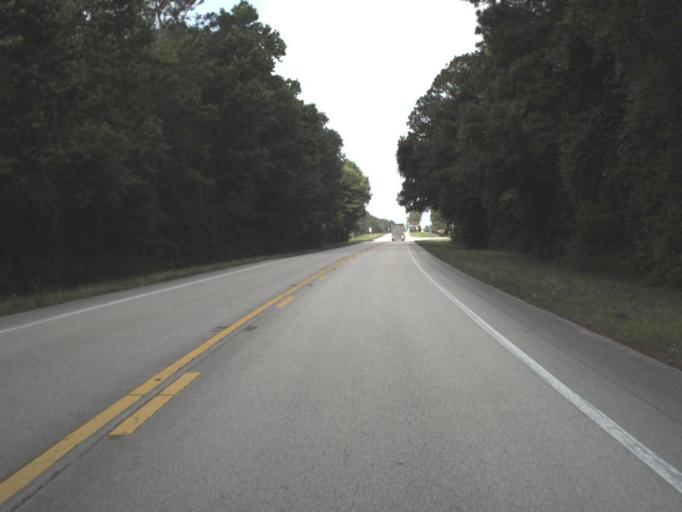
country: US
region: Florida
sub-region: Saint Johns County
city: Saint Augustine Shores
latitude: 29.7262
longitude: -81.4220
